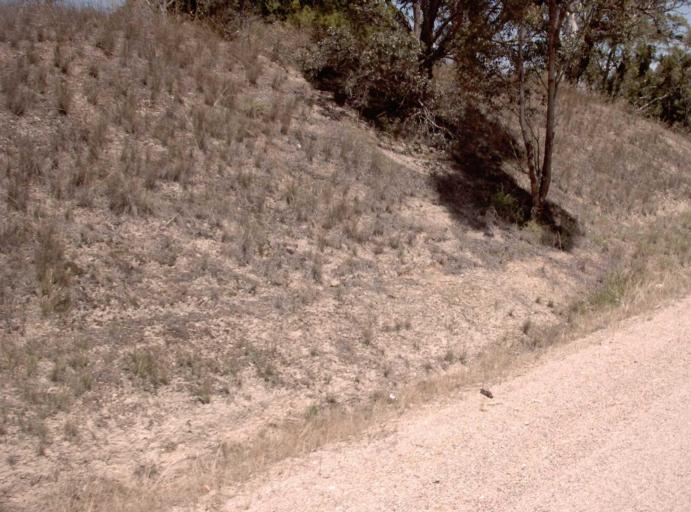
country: AU
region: Victoria
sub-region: East Gippsland
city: Bairnsdale
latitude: -37.7599
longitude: 147.7054
